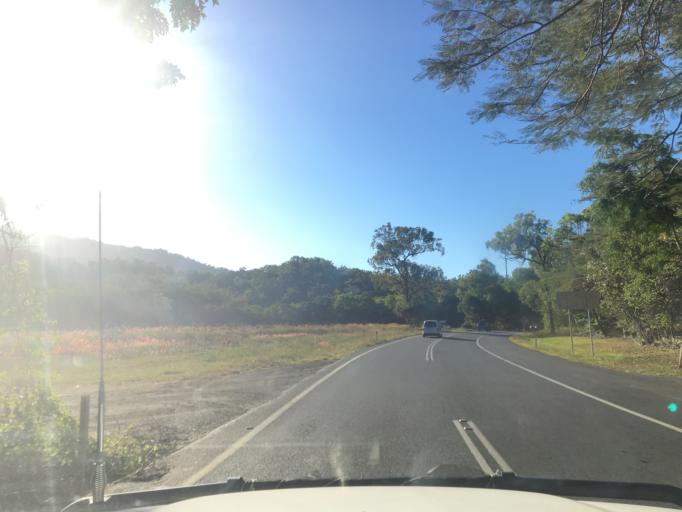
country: AU
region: Queensland
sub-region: Cairns
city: Port Douglas
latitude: -16.5907
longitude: 145.5140
